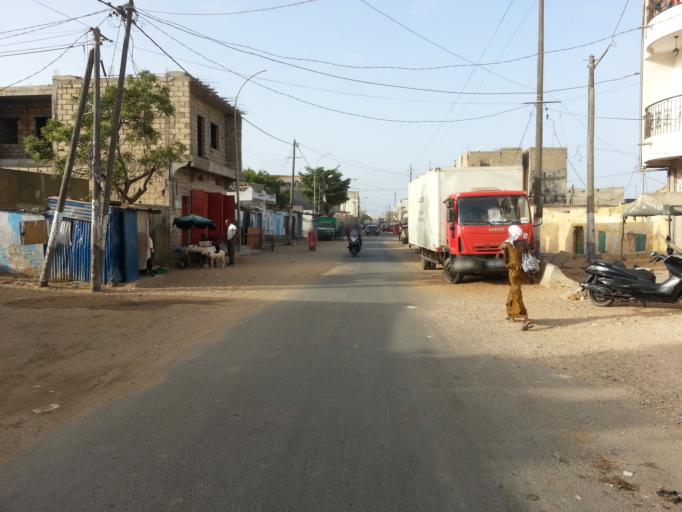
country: SN
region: Dakar
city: Pikine
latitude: 14.7658
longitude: -17.3855
